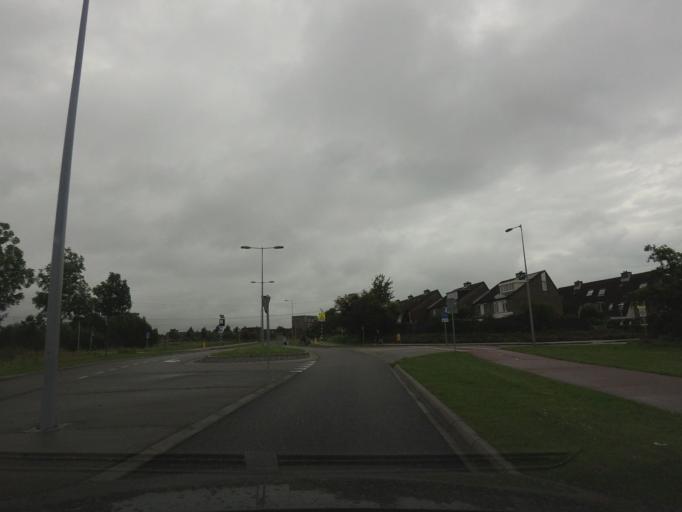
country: NL
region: North Holland
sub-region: Gemeente Haarlemmermeer
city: Hoofddorp
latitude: 52.3124
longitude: 4.6463
